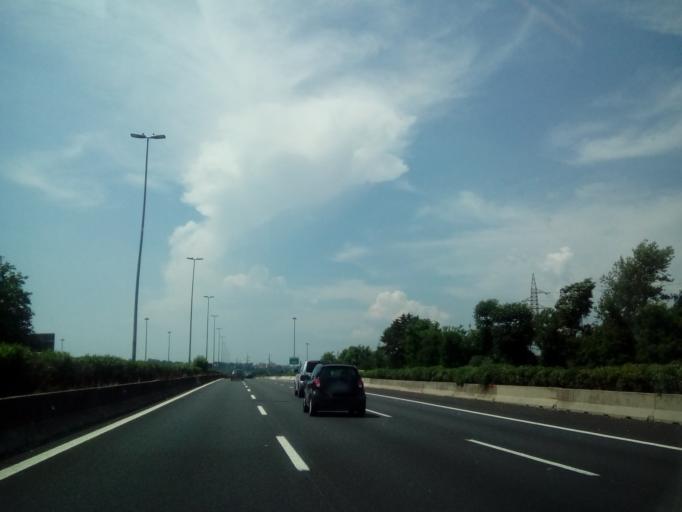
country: IT
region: Latium
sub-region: Citta metropolitana di Roma Capitale
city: Monte Caminetto
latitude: 41.9876
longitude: 12.5163
